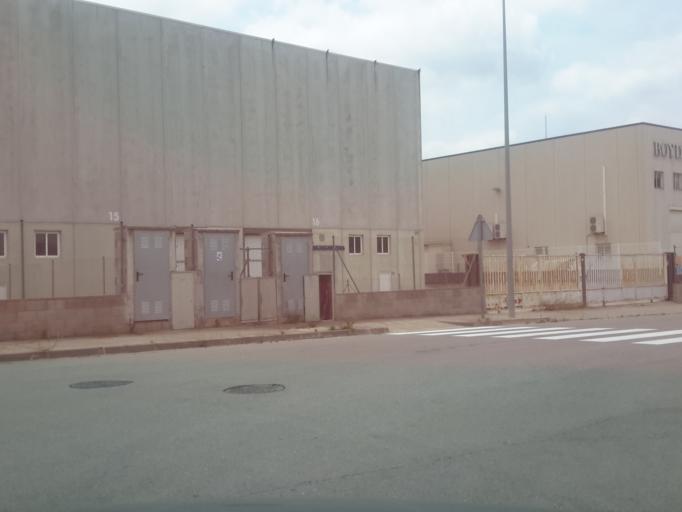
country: ES
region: Catalonia
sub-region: Provincia de Barcelona
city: Avinyonet del Penedes
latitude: 41.3611
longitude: 1.7627
